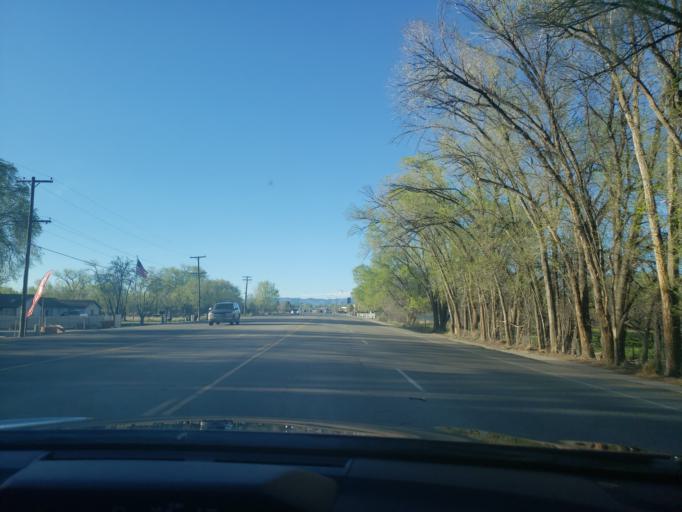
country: US
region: Colorado
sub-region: Mesa County
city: Fruita
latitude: 39.1477
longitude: -108.7382
